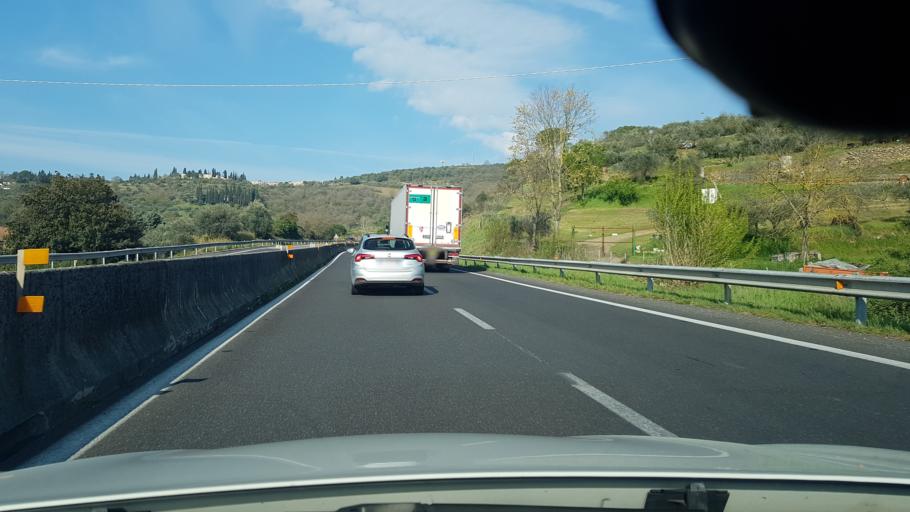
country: IT
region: Umbria
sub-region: Provincia di Perugia
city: Magione
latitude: 43.1518
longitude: 12.2140
